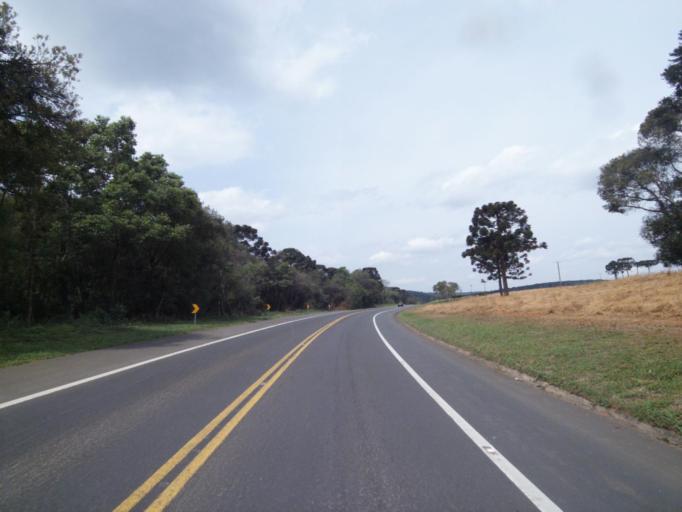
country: BR
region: Parana
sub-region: Irati
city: Irati
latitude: -25.4524
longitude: -50.4525
